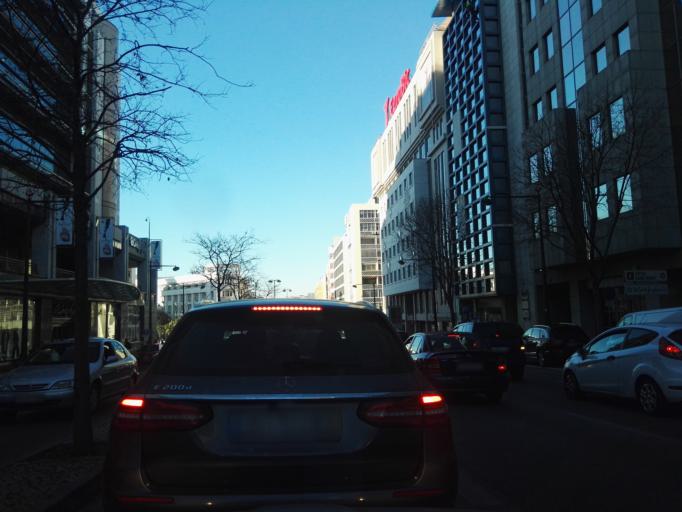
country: PT
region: Lisbon
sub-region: Lisbon
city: Lisbon
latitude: 38.7334
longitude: -9.1532
